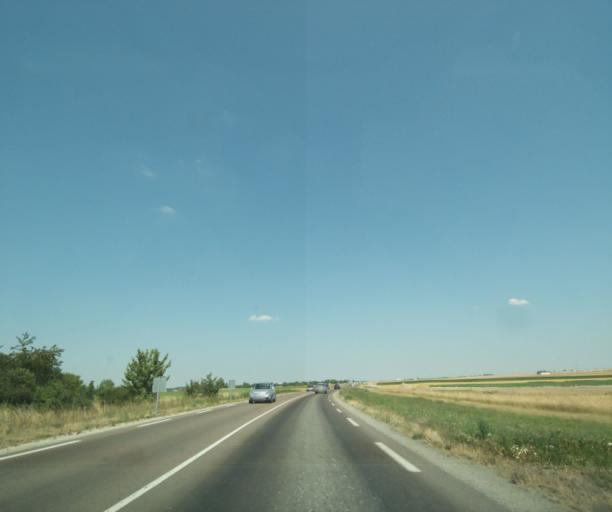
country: FR
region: Champagne-Ardenne
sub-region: Departement de la Marne
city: Sarry
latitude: 48.9122
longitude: 4.4285
